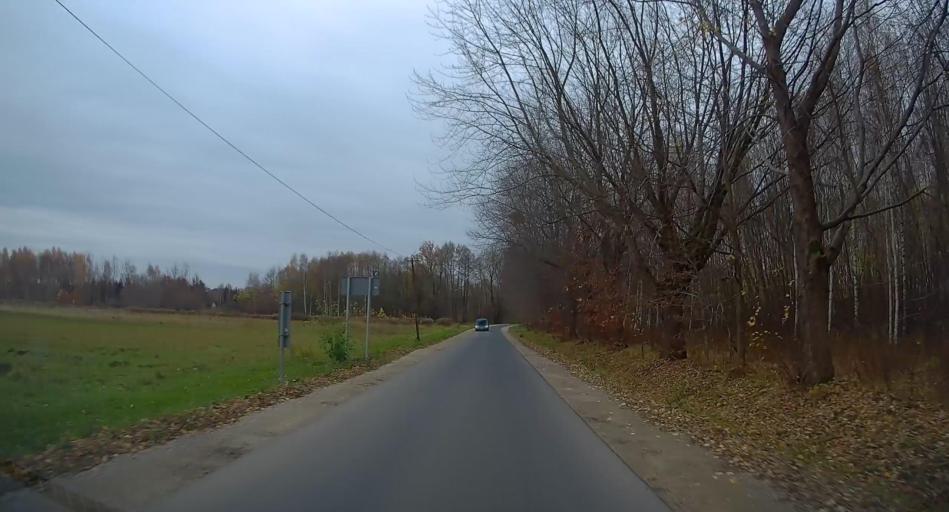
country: PL
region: Lodz Voivodeship
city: Zabia Wola
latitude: 52.0193
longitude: 20.6556
